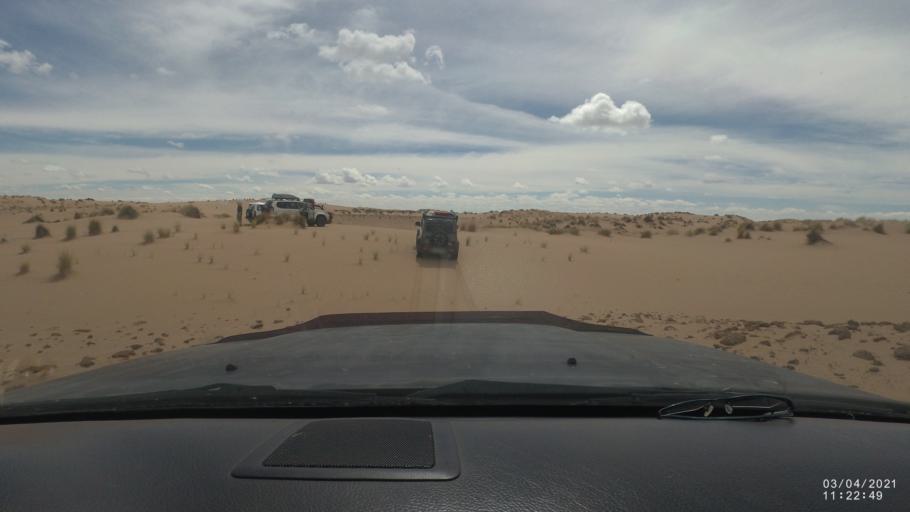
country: BO
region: Oruro
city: Poopo
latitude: -18.7030
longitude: -67.5114
